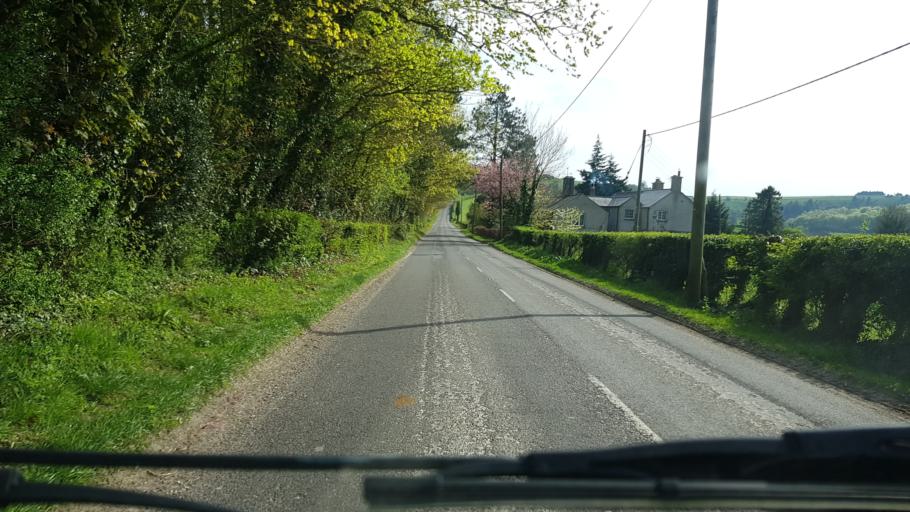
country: GB
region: England
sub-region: Hampshire
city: Kingsclere
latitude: 51.3147
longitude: -1.2535
